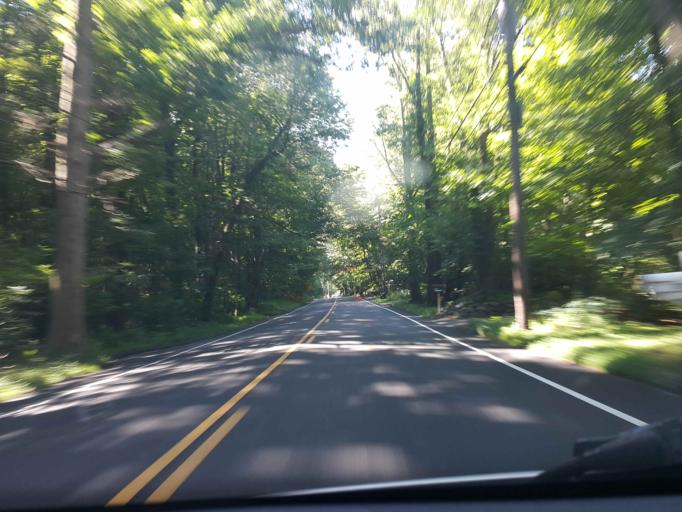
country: US
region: Connecticut
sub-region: New Haven County
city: North Branford
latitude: 41.3471
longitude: -72.7165
